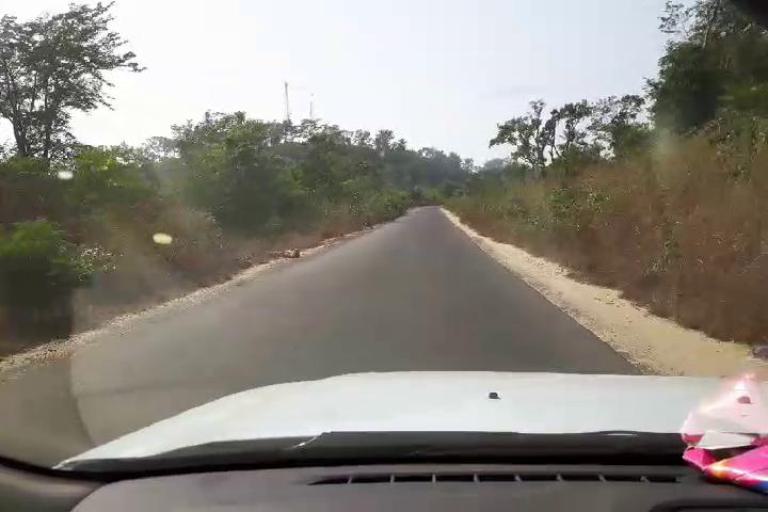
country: SL
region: Western Area
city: Waterloo
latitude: 8.2622
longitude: -13.1608
